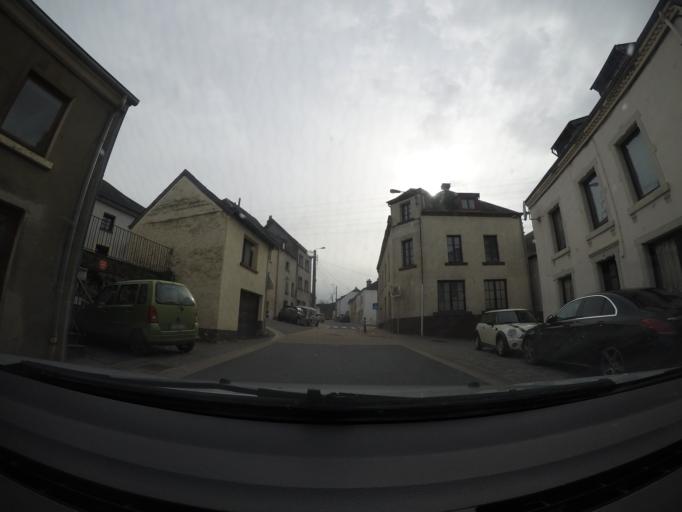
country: BE
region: Wallonia
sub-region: Province du Luxembourg
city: Martelange
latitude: 49.8309
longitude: 5.7377
